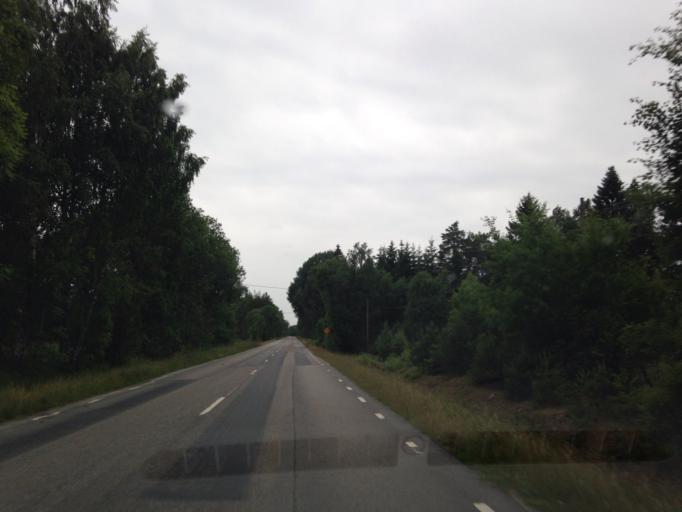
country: SE
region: Vaestra Goetaland
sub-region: Harryda Kommun
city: Hindas
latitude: 57.6730
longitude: 12.3499
